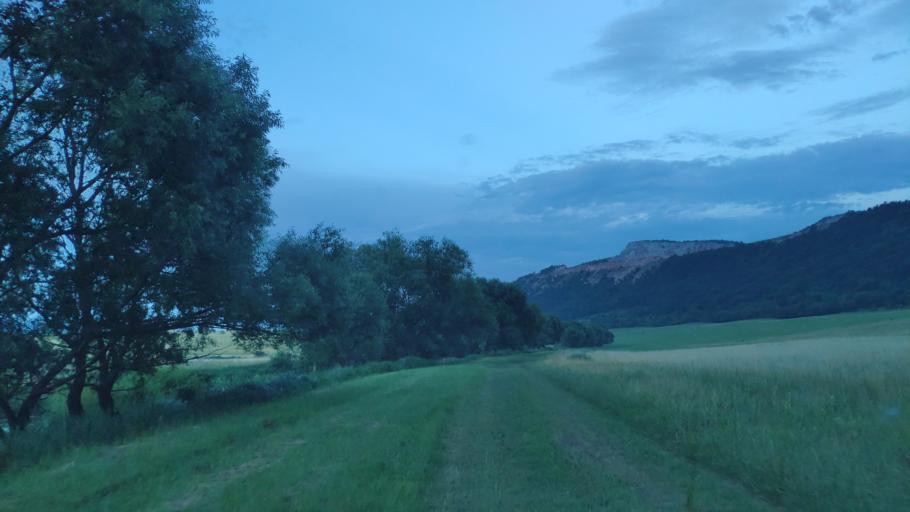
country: SK
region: Kosicky
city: Medzev
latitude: 48.5831
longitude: 20.7898
